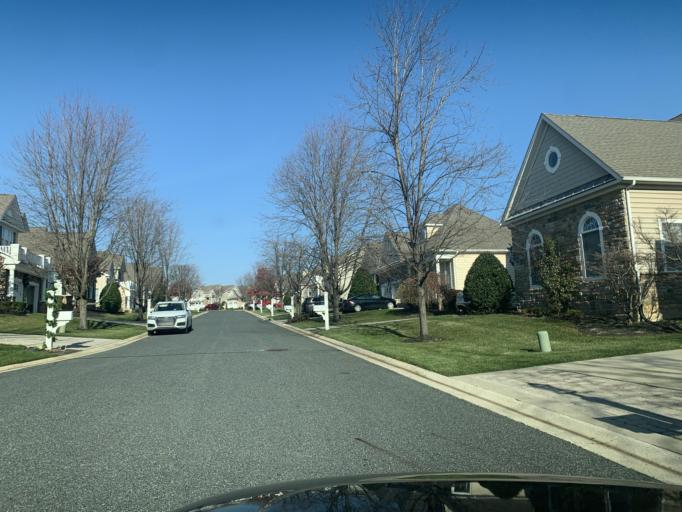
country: US
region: Maryland
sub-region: Harford County
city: Havre de Grace
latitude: 39.5502
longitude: -76.1270
